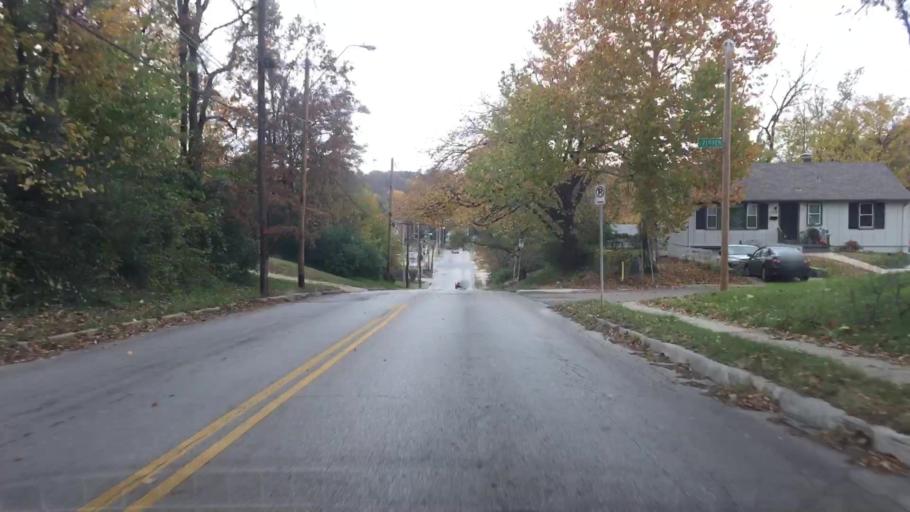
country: US
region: Kansas
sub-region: Johnson County
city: Mission Hills
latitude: 38.9965
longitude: -94.5430
